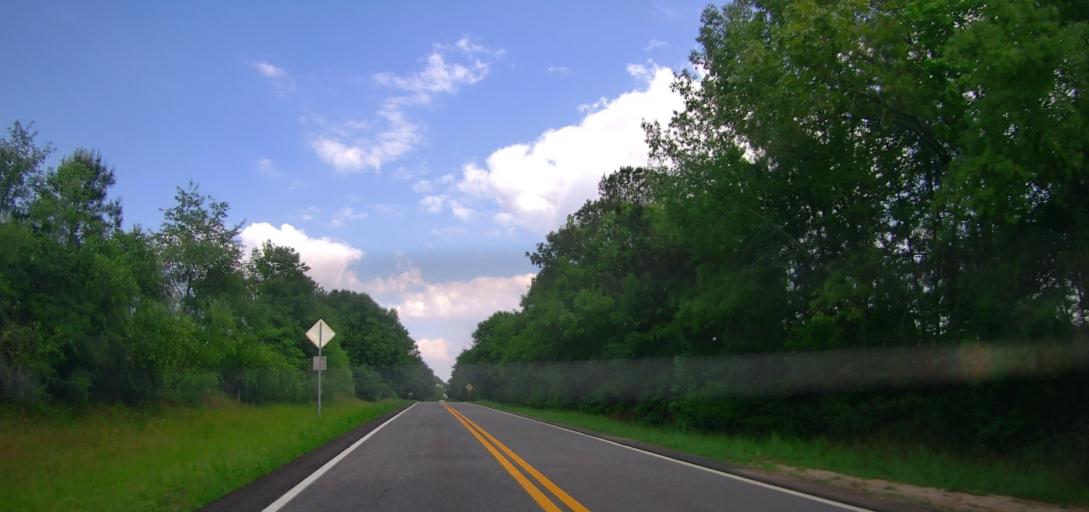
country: US
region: Georgia
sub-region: Laurens County
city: East Dublin
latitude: 32.6317
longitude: -82.8921
